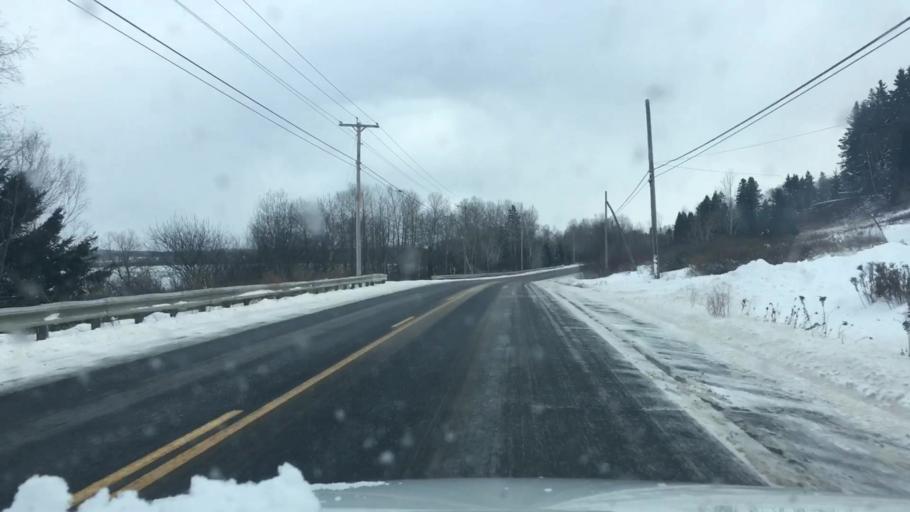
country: US
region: Maine
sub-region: Aroostook County
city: Madawaska
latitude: 47.3241
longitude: -68.1734
